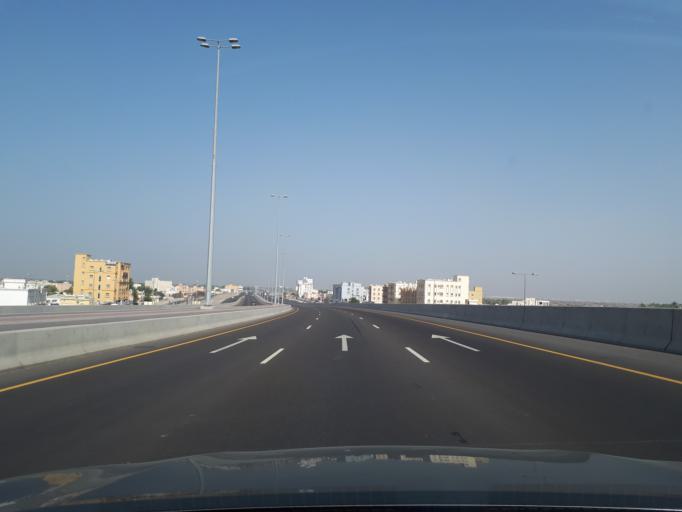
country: OM
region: Al Batinah
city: Al Liwa'
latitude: 24.4229
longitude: 56.6132
